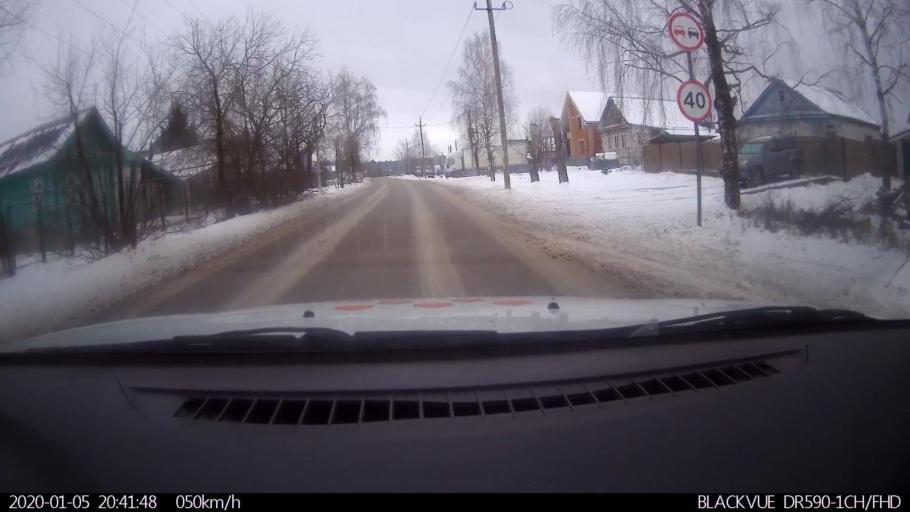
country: RU
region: Nizjnij Novgorod
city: Lukino
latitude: 56.4006
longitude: 43.7295
